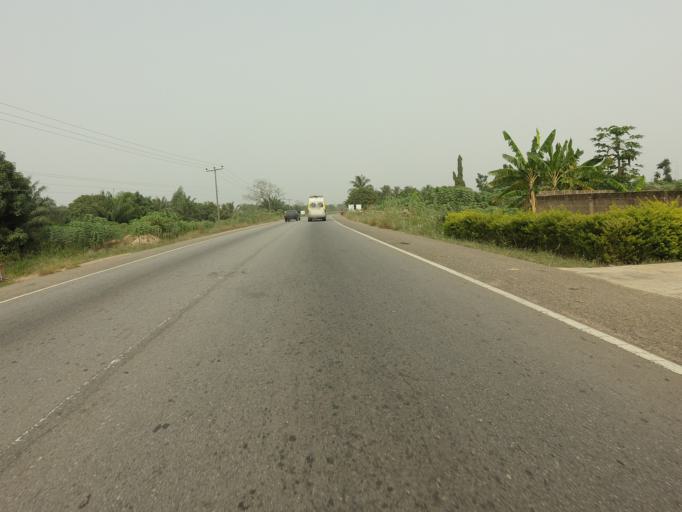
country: GH
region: Volta
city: Anloga
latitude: 5.9963
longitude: 0.5654
